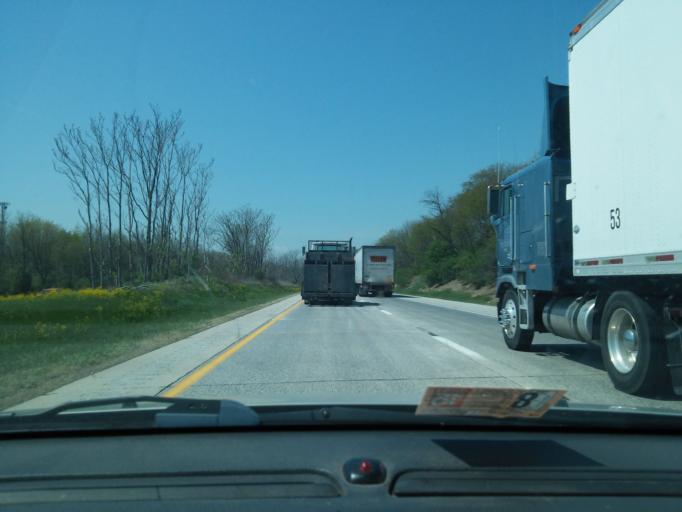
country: US
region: Pennsylvania
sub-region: Lebanon County
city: Jonestown
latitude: 40.4434
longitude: -76.4743
